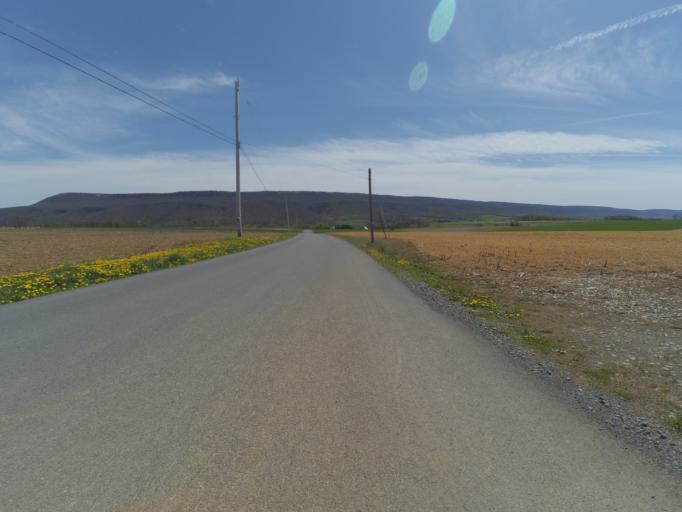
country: US
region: Pennsylvania
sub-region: Blair County
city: Tyrone
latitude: 40.6126
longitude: -78.2302
